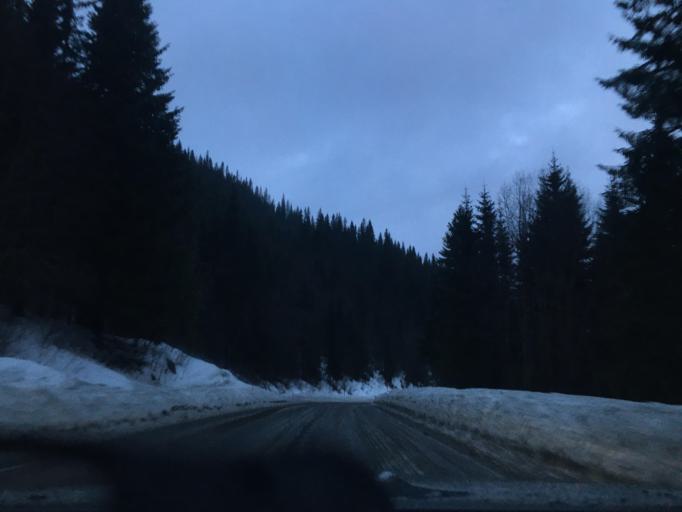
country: NO
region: Nordland
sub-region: Rana
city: Hauknes
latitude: 66.2872
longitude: 13.9076
